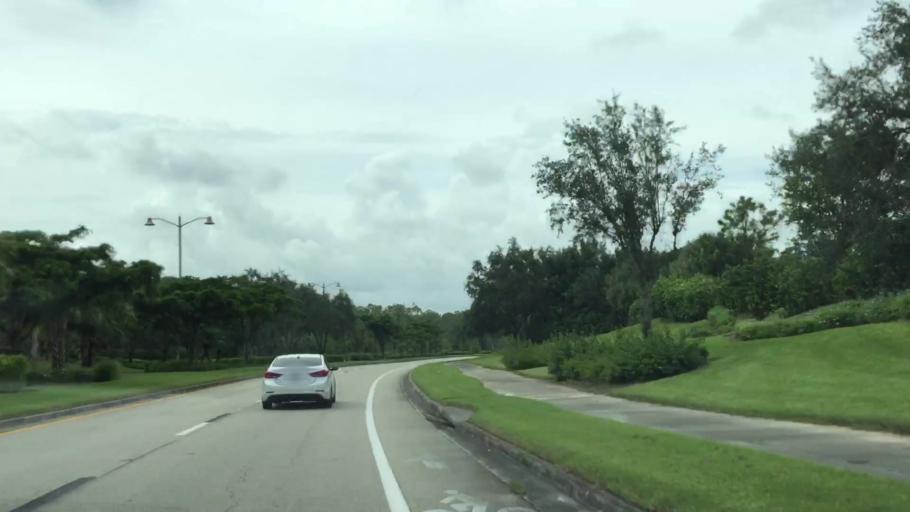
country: US
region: Florida
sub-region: Lee County
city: Estero
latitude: 26.4150
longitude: -81.7873
